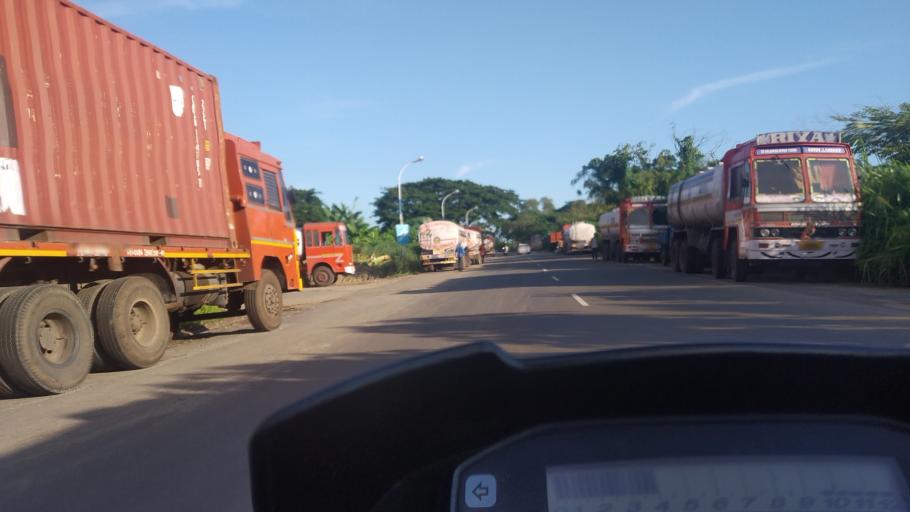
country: IN
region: Kerala
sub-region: Ernakulam
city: Cochin
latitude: 9.9373
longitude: 76.2703
